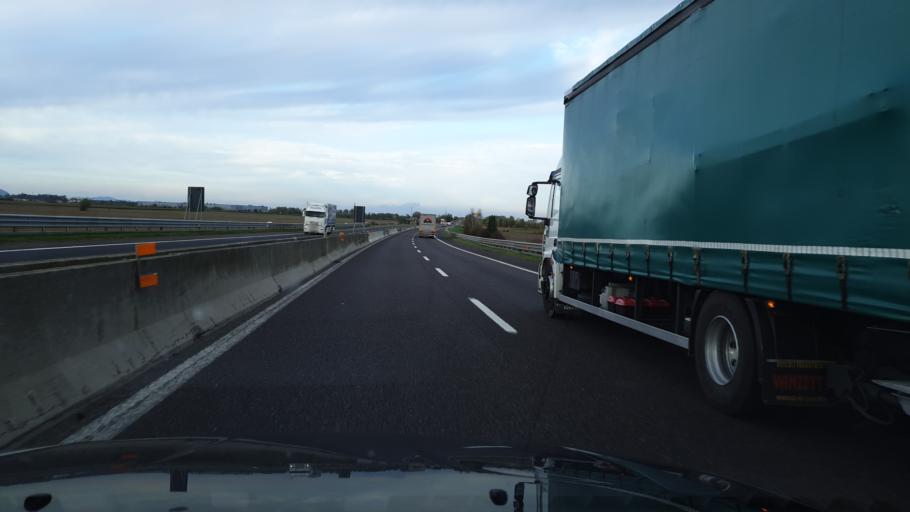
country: IT
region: Veneto
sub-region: Provincia di Padova
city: Boara Pisani
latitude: 45.1033
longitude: 11.7553
